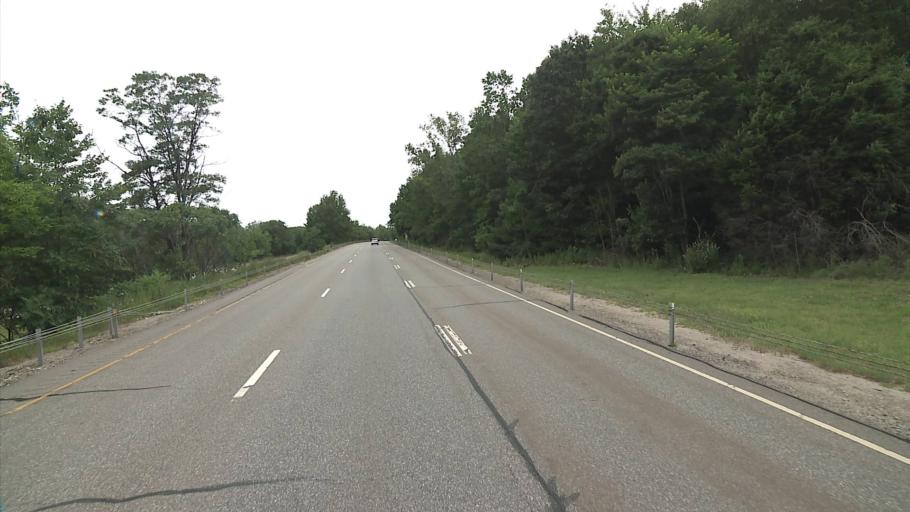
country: US
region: Connecticut
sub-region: Litchfield County
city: Torrington
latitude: 41.8449
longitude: -73.0949
